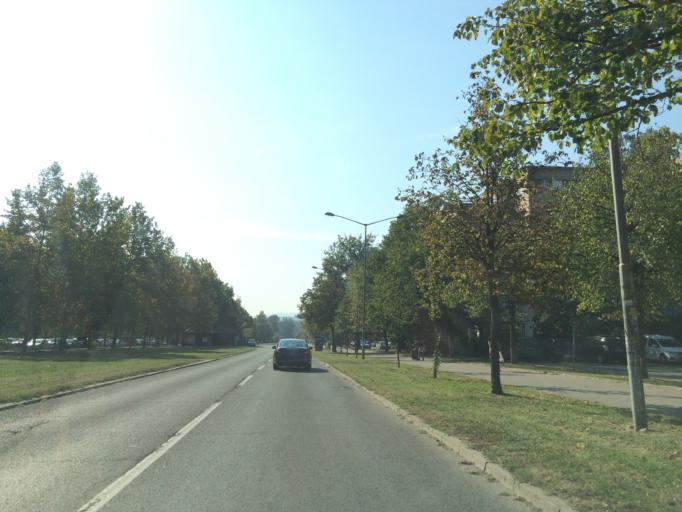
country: RS
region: Autonomna Pokrajina Vojvodina
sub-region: Juznobacki Okrug
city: Novi Sad
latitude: 45.2403
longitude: 19.8316
